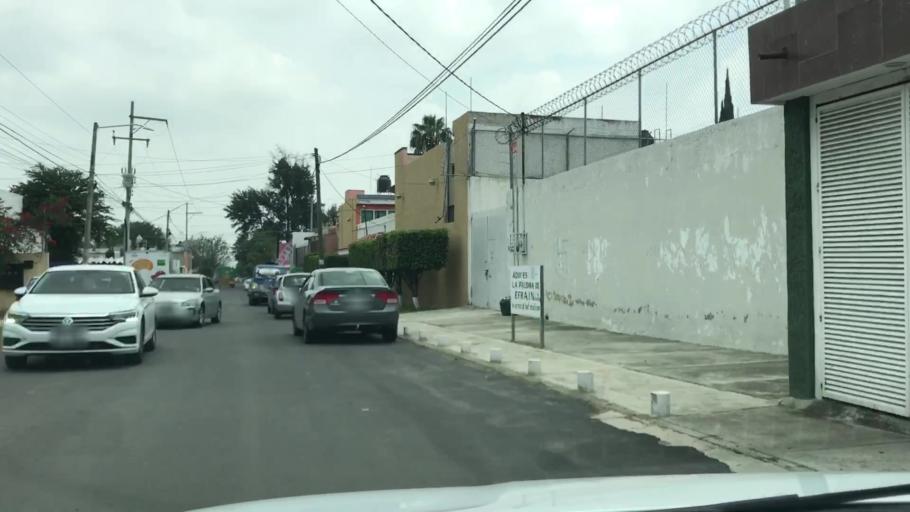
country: MX
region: Jalisco
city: Guadalajara
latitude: 20.6442
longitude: -103.4351
